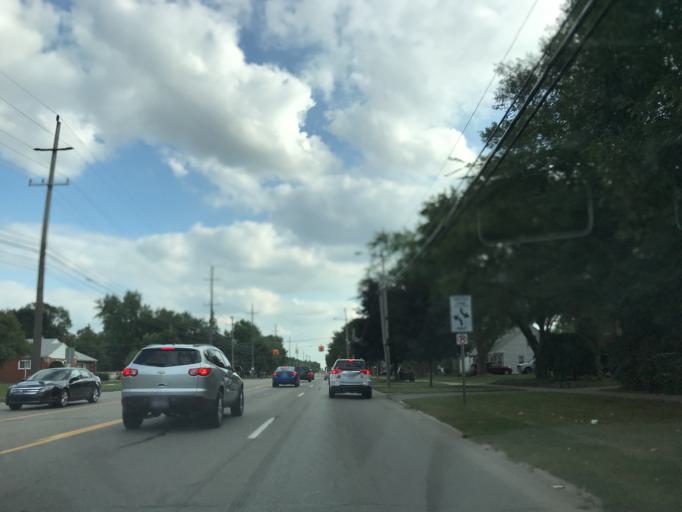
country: US
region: Michigan
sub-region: Wayne County
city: Redford
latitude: 42.3909
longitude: -83.2957
